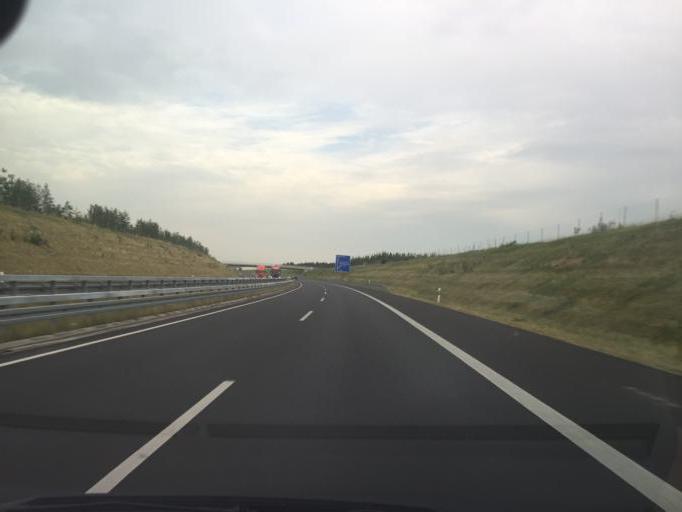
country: NL
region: Limburg
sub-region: Gemeente Venlo
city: Venlo
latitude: 51.3322
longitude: 6.1748
